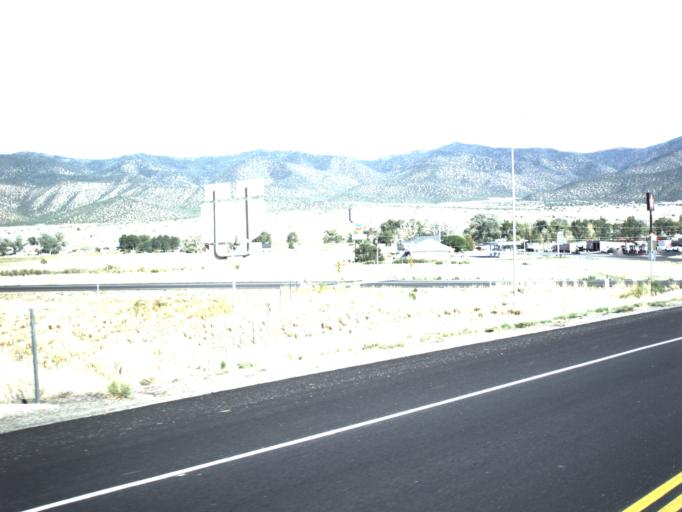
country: US
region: Utah
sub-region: Sanpete County
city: Gunnison
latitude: 39.2525
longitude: -112.1137
